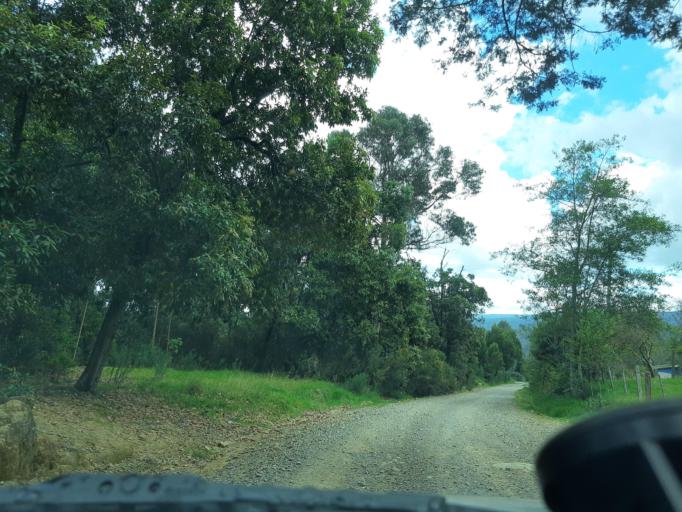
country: CO
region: Boyaca
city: Raquira
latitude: 5.5059
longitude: -73.6727
